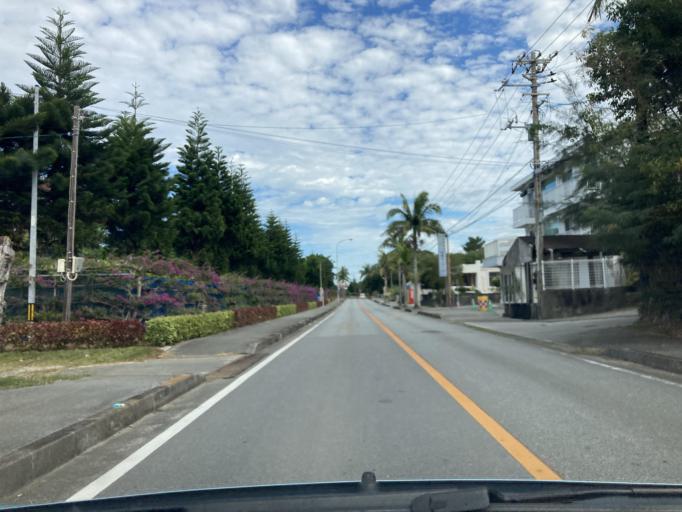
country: JP
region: Okinawa
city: Ishikawa
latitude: 26.4251
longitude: 127.7476
